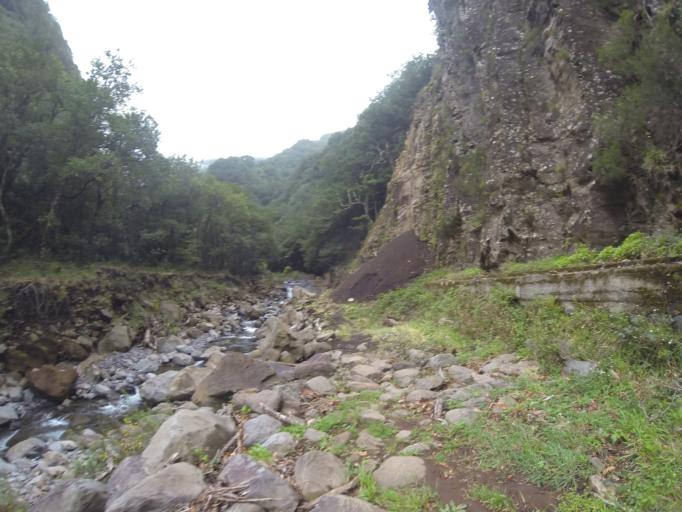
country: PT
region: Madeira
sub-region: Sao Vicente
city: Sao Vicente
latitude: 32.7924
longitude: -17.1136
